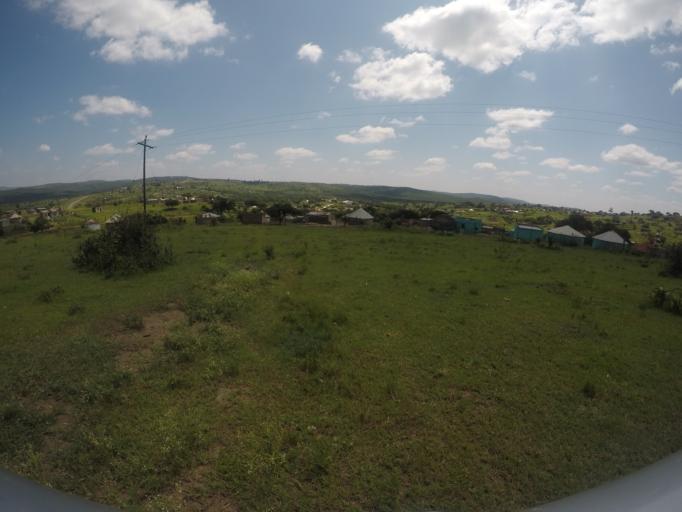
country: ZA
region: KwaZulu-Natal
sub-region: uThungulu District Municipality
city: Empangeni
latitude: -28.6002
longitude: 31.7345
